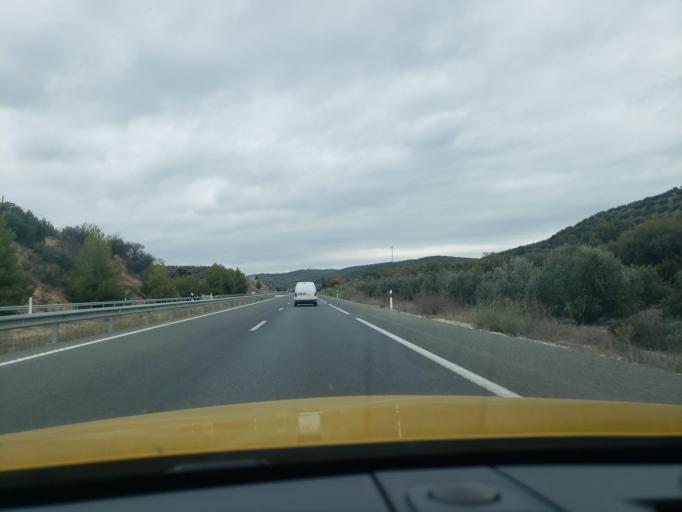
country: ES
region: Andalusia
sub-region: Provincia de Granada
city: Deifontes
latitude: 37.3347
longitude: -3.6290
